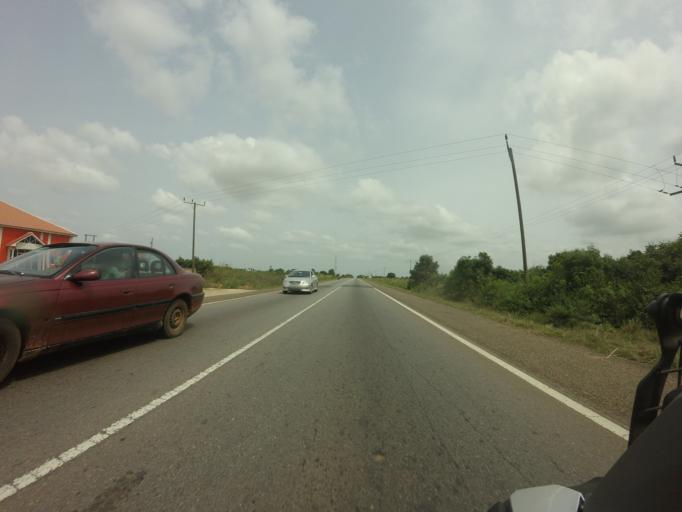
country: GH
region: Volta
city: Anloga
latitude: 5.9295
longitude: 0.5233
